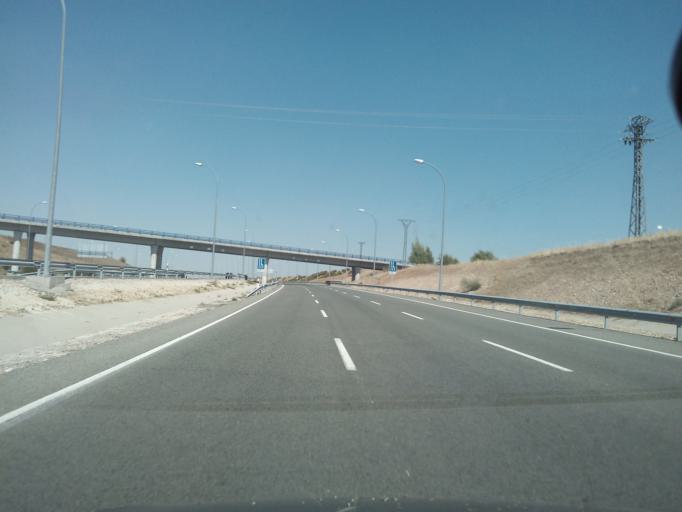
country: ES
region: Madrid
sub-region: Provincia de Madrid
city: Torrejon de Ardoz
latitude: 40.4657
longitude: -3.5098
